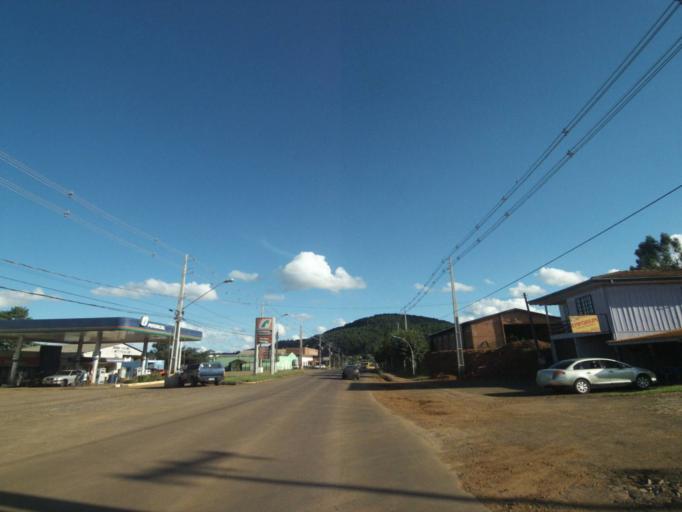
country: BR
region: Parana
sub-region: Uniao Da Vitoria
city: Uniao da Vitoria
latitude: -26.1632
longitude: -51.5370
